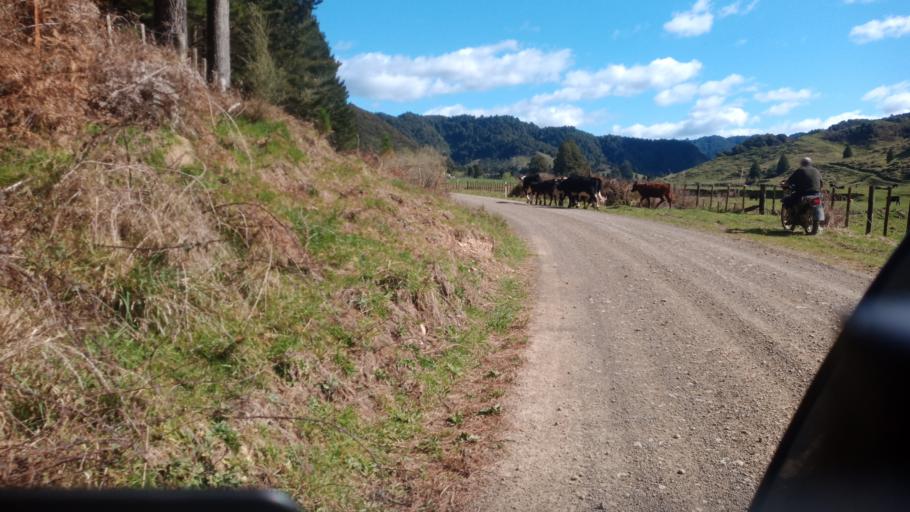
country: NZ
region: Bay of Plenty
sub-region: Opotiki District
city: Opotiki
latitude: -38.1096
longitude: 177.5243
